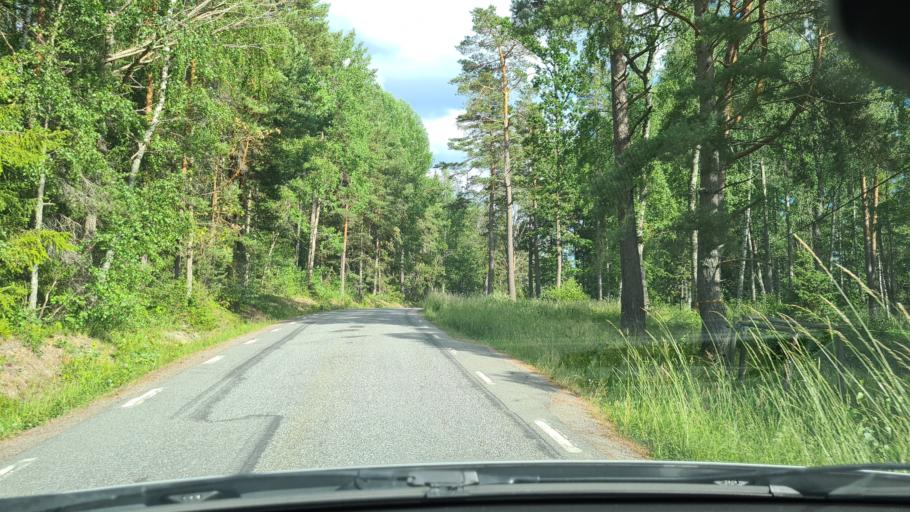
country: SE
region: Stockholm
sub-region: Vaxholms Kommun
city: Vaxholm
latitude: 59.4122
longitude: 18.4457
